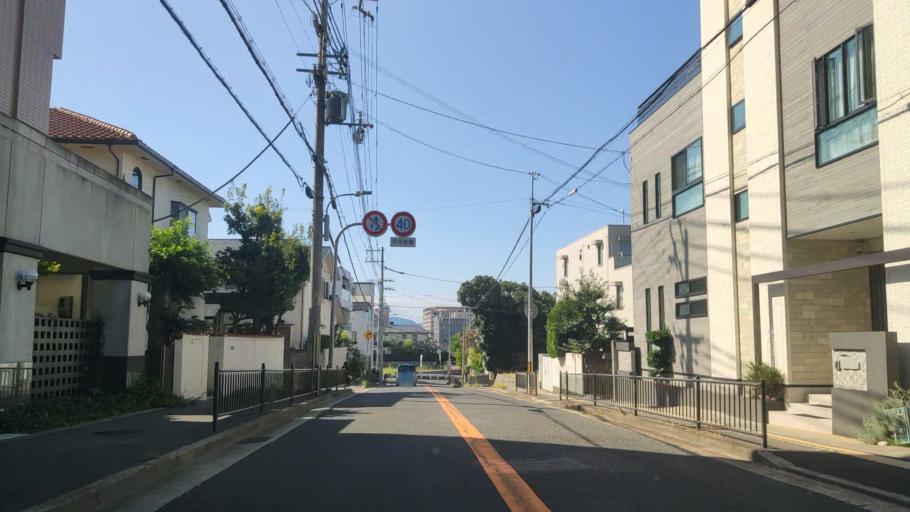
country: JP
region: Hyogo
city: Akashi
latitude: 34.6526
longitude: 134.9973
